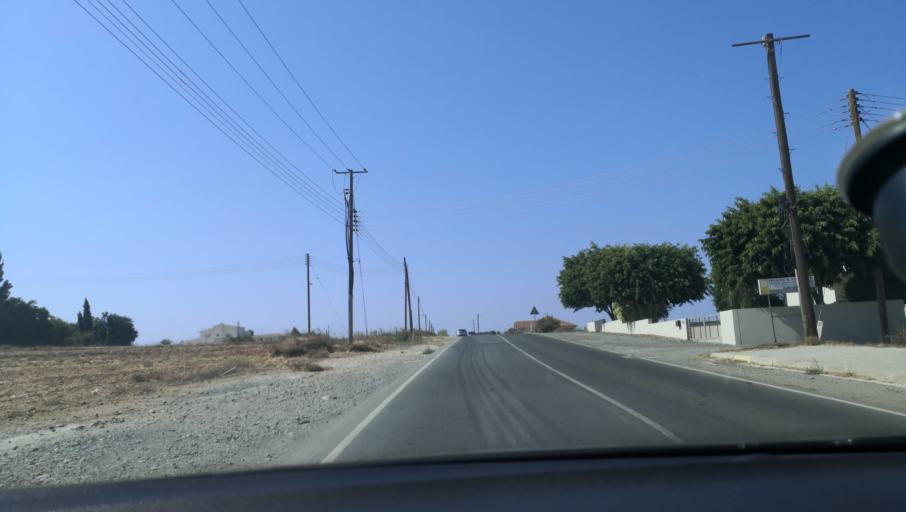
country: CY
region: Lefkosia
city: Kokkinotrimithia
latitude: 35.1158
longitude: 33.2254
